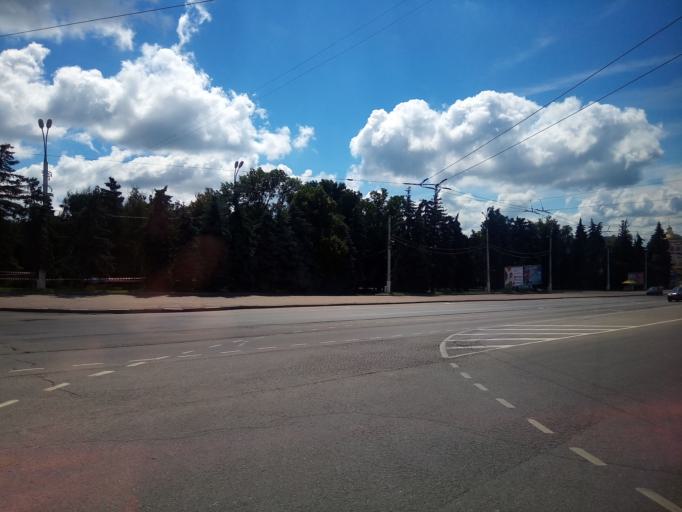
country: RU
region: Kursk
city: Kursk
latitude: 51.7303
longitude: 36.1925
